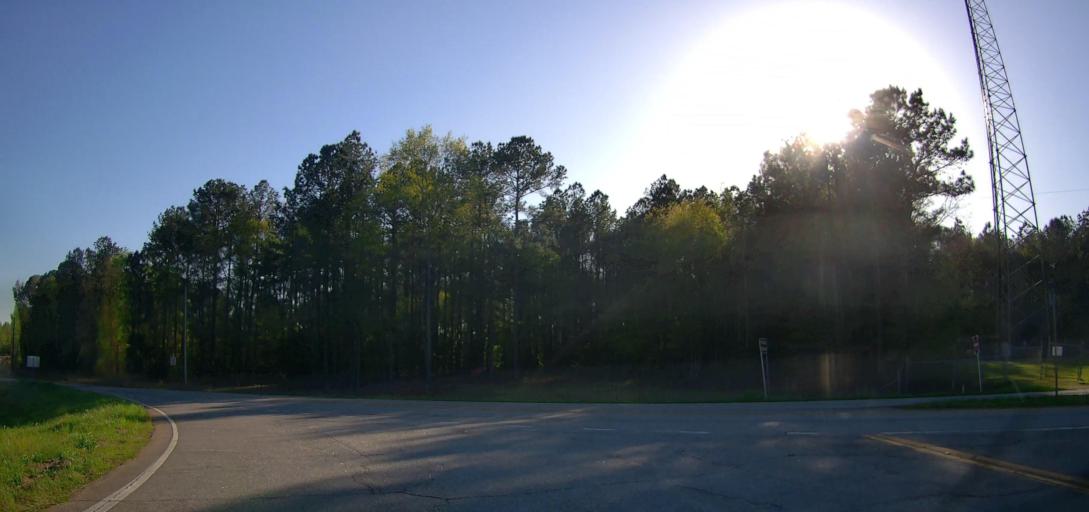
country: US
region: Georgia
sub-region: Butts County
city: Indian Springs
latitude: 33.2635
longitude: -83.9089
